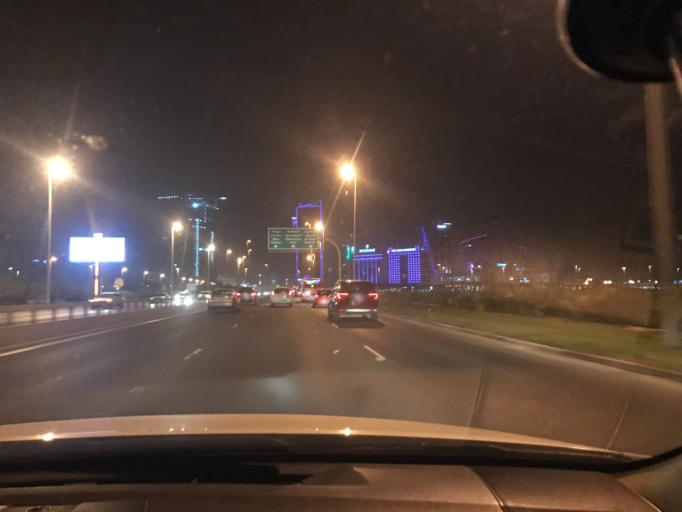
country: BH
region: Muharraq
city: Al Muharraq
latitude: 26.2459
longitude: 50.6003
